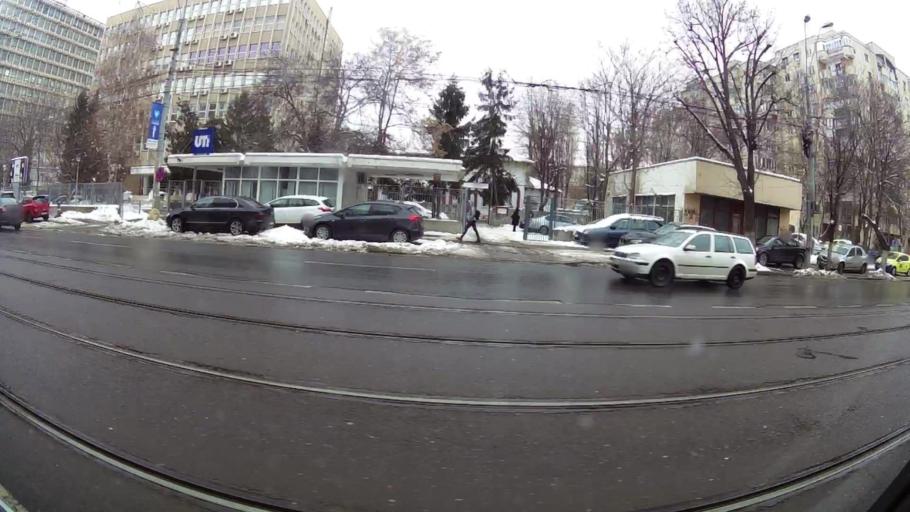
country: RO
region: Ilfov
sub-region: Comuna Popesti-Leordeni
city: Popesti-Leordeni
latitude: 44.3917
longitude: 26.1263
